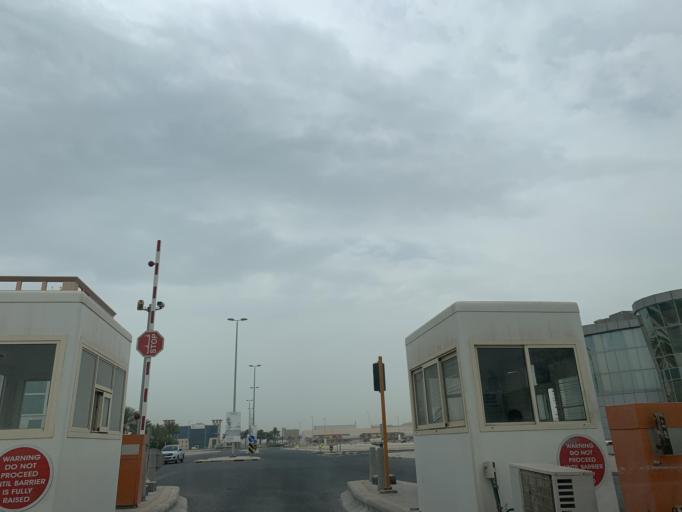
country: BH
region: Muharraq
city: Al Hadd
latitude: 26.2240
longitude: 50.6740
